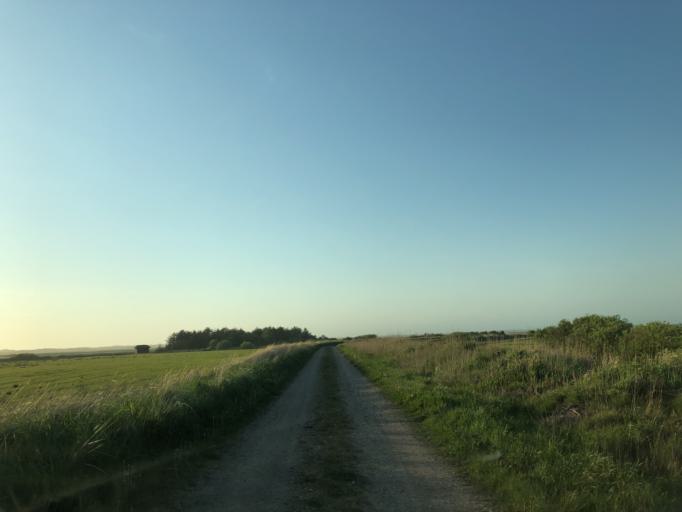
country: DK
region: Central Jutland
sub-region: Ringkobing-Skjern Kommune
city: Ringkobing
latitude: 56.2042
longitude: 8.1606
